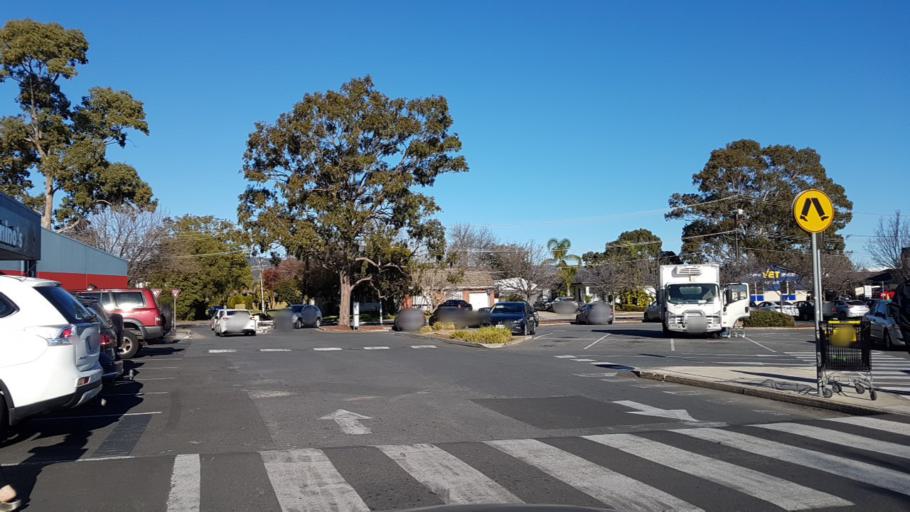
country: AU
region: South Australia
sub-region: Campbelltown
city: Paradise
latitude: -34.8779
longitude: 138.6746
